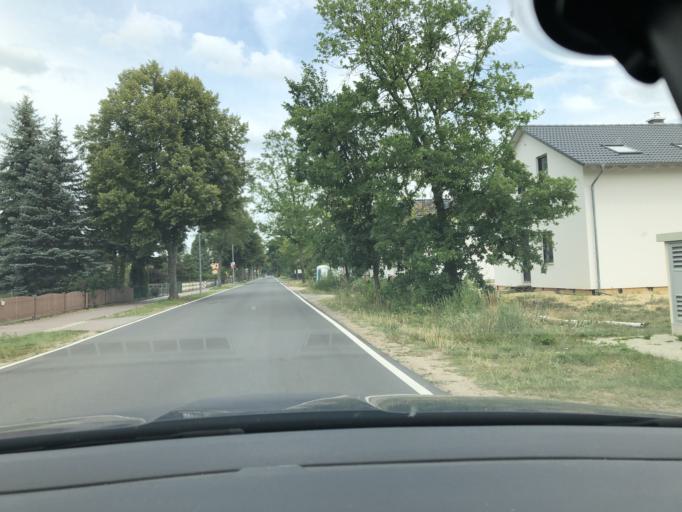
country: DE
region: Brandenburg
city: Kasel-Golzig
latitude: 51.9854
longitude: 13.7733
